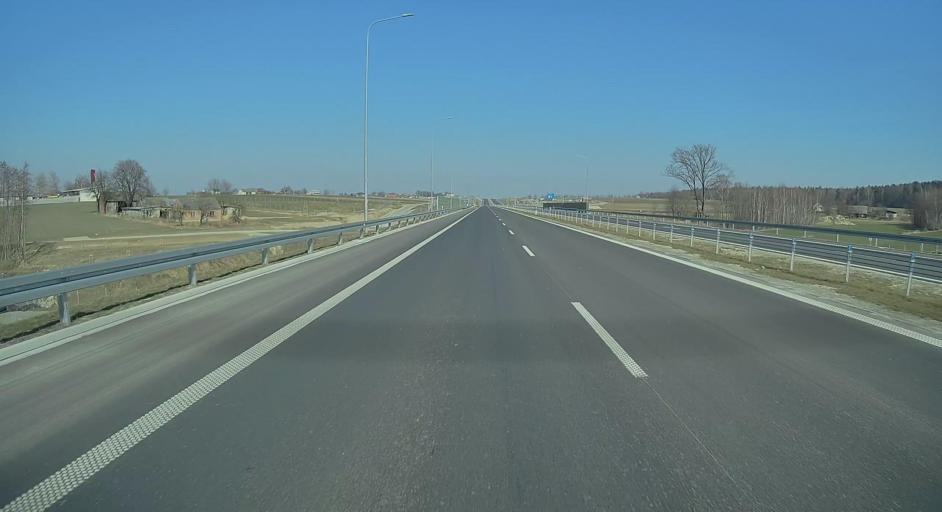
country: PL
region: Lublin Voivodeship
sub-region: Powiat janowski
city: Modliborzyce
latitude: 50.7749
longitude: 22.2918
